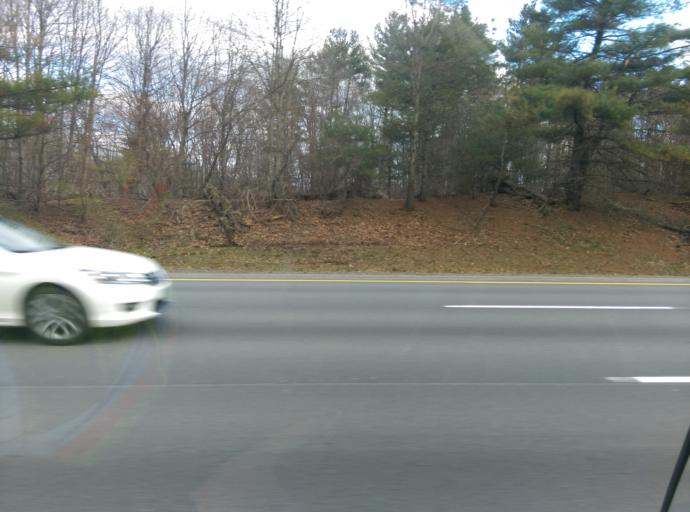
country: US
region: Massachusetts
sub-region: Middlesex County
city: Tewksbury
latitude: 42.6573
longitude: -71.2039
